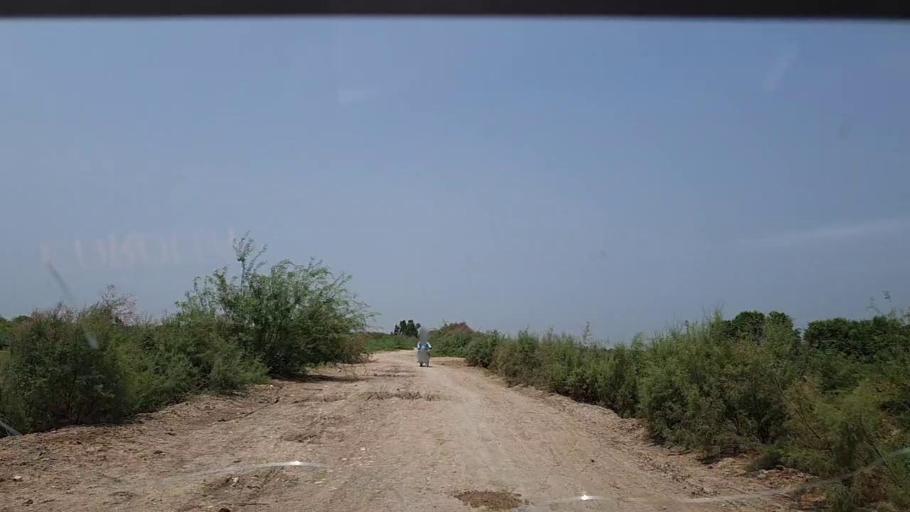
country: PK
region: Sindh
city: Adilpur
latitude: 27.9010
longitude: 69.2316
